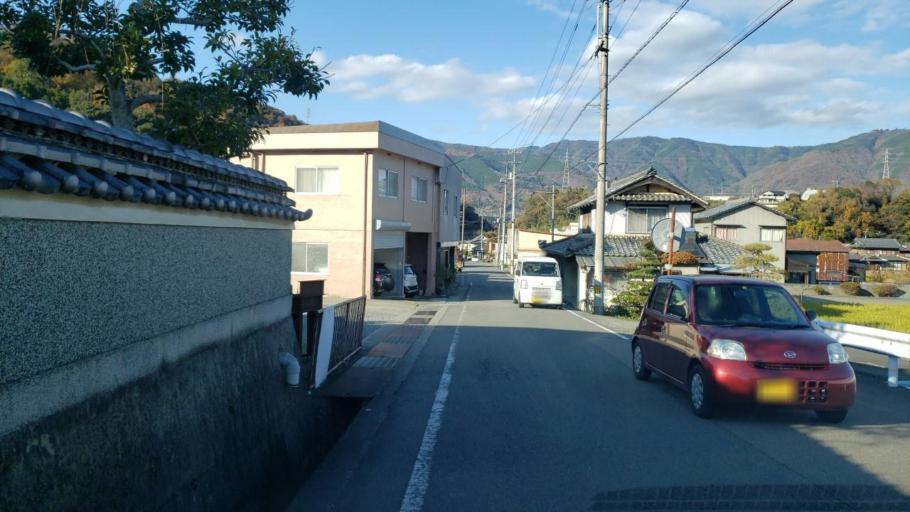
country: JP
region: Tokushima
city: Wakimachi
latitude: 34.0339
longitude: 134.0291
